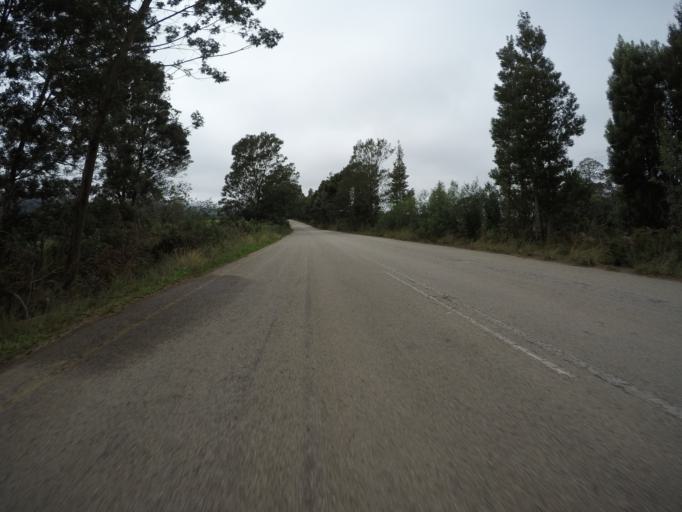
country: ZA
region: Eastern Cape
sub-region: Cacadu District Municipality
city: Kareedouw
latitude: -33.9970
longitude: 24.1526
